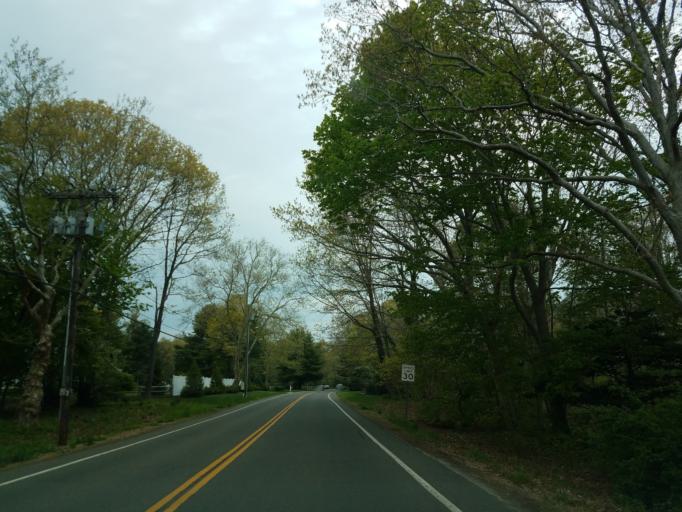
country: US
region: Connecticut
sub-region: Middlesex County
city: Old Saybrook Center
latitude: 41.2677
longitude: -72.3643
